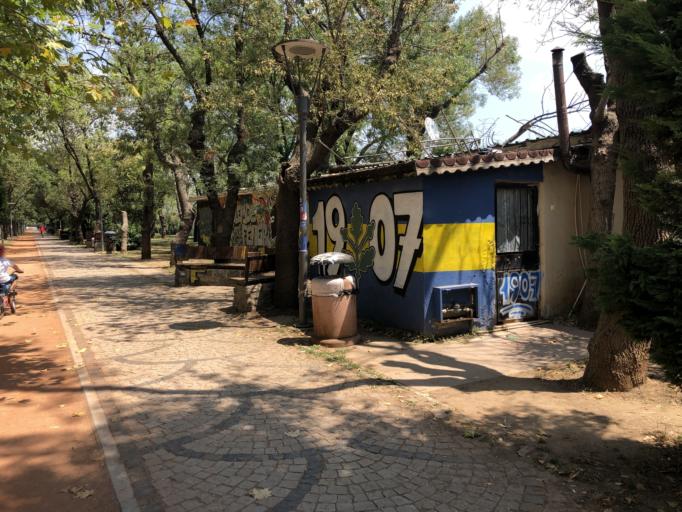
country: TR
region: Istanbul
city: UEskuedar
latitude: 40.9836
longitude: 29.0337
